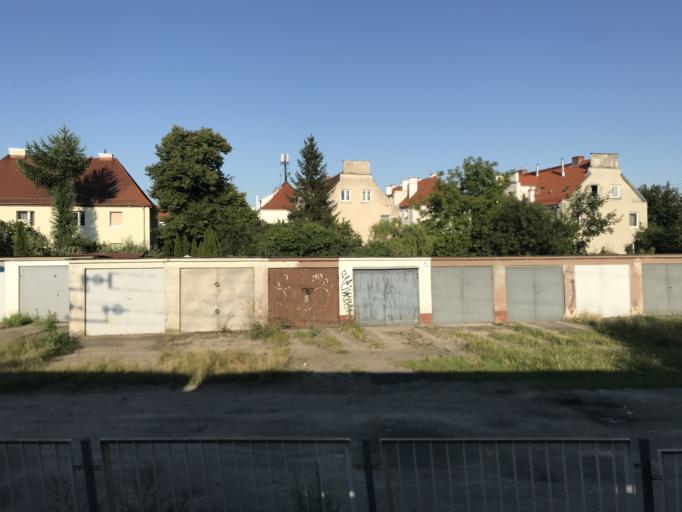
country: PL
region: Pomeranian Voivodeship
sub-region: Gdansk
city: Gdansk
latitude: 54.3207
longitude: 18.6334
